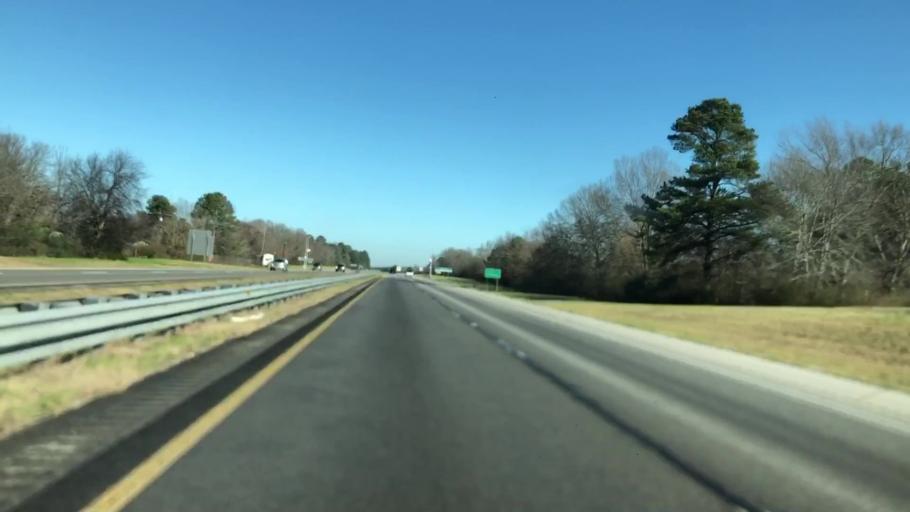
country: US
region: Alabama
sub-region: Limestone County
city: Athens
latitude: 34.8423
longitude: -86.9339
